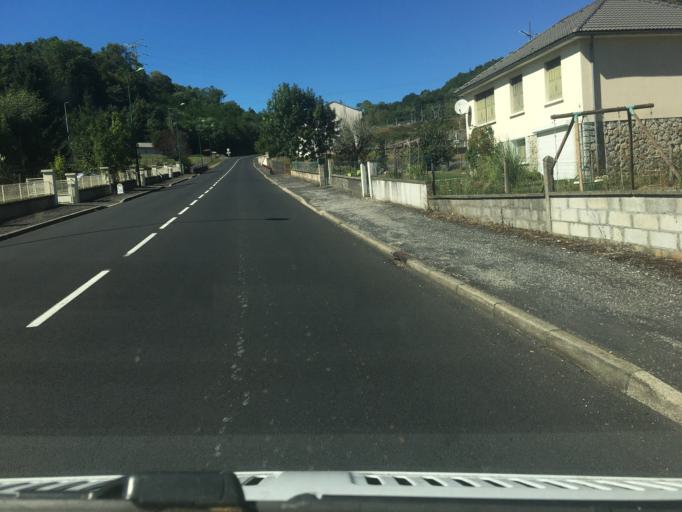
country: FR
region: Limousin
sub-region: Departement de la Correze
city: Bort-les-Orgues
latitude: 45.4131
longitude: 2.5048
